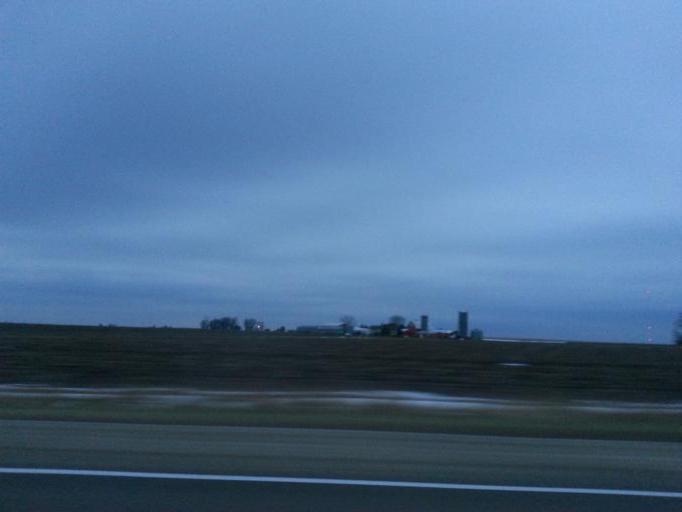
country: US
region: Iowa
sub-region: Black Hawk County
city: La Porte City
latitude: 42.3917
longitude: -92.1366
